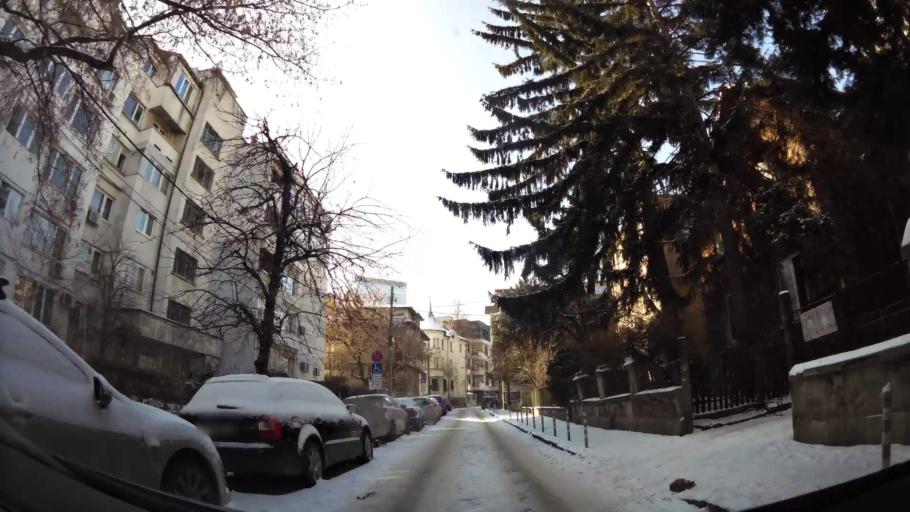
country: BG
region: Sofia-Capital
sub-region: Stolichna Obshtina
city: Sofia
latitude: 42.6800
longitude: 23.3238
